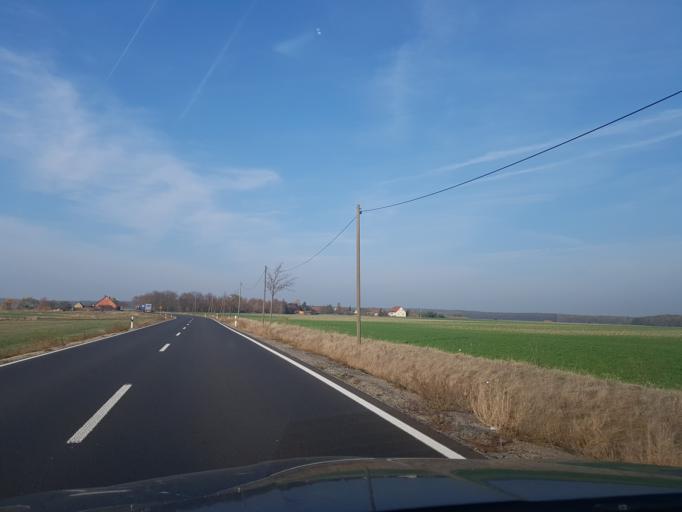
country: DE
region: Saxony
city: Arzberg
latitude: 51.5467
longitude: 13.1628
